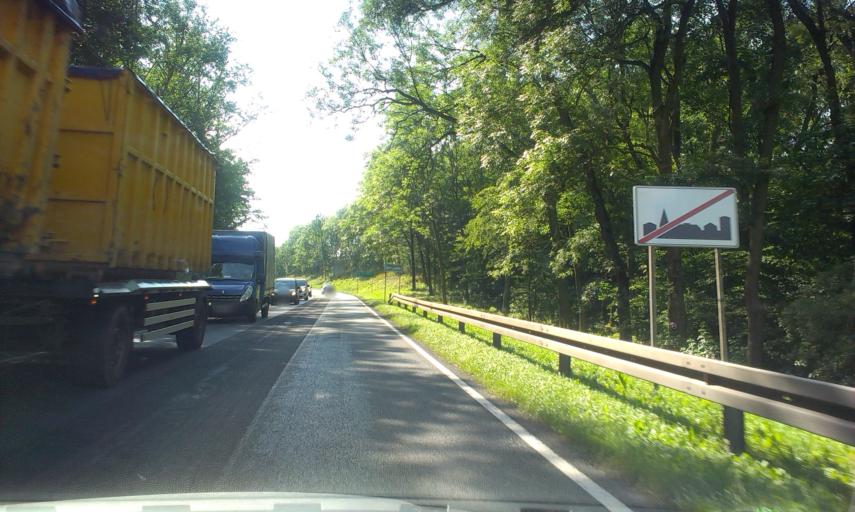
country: PL
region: Kujawsko-Pomorskie
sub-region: Powiat bydgoski
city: Sicienko
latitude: 53.1674
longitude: 17.7716
